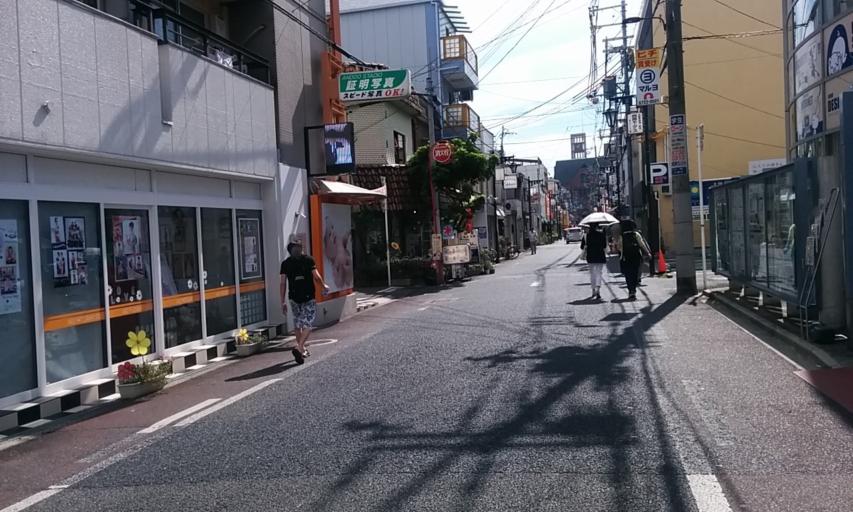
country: JP
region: Osaka
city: Yao
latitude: 34.6514
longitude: 135.5827
